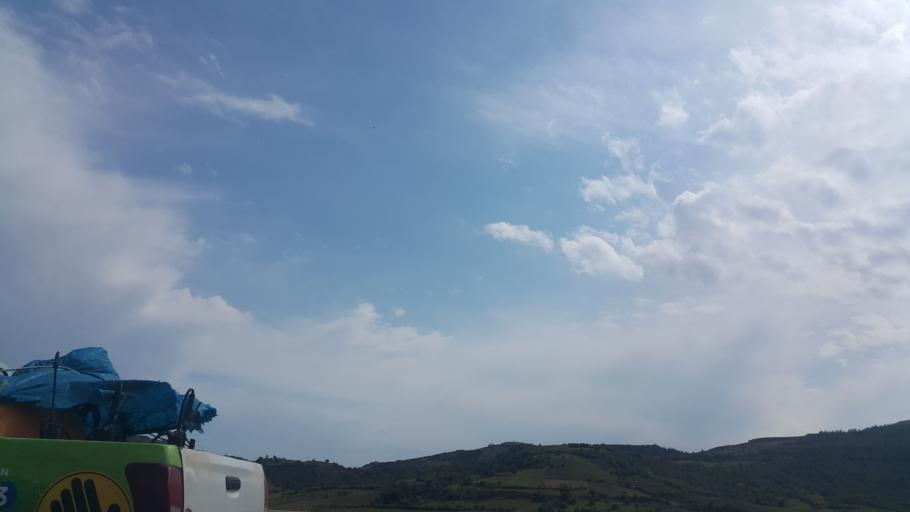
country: TR
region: Mersin
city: Tarsus
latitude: 36.9507
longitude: 34.7744
